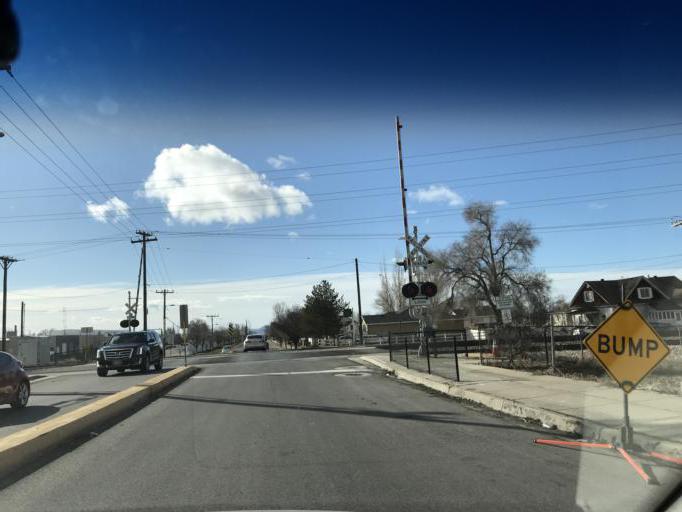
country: US
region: Utah
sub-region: Davis County
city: Woods Cross
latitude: 40.8748
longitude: -111.9052
